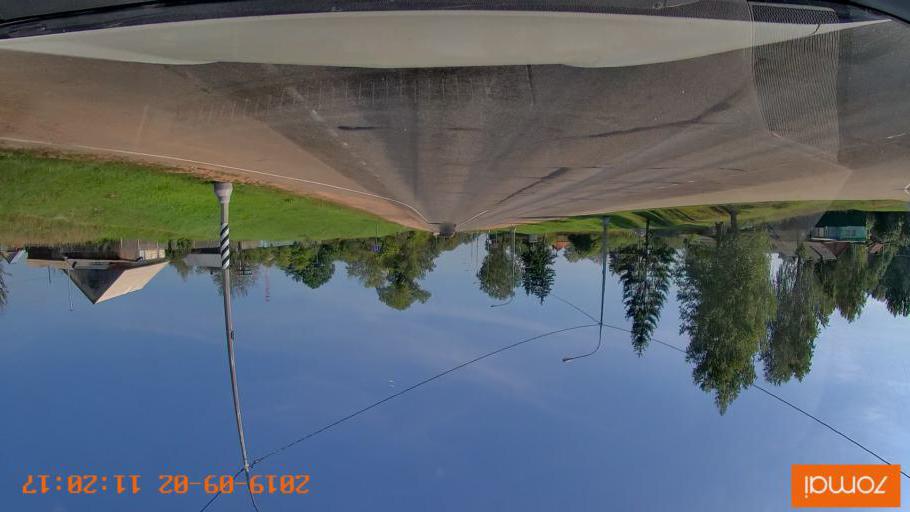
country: RU
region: Smolensk
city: Roslavl'
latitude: 54.0425
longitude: 33.0551
